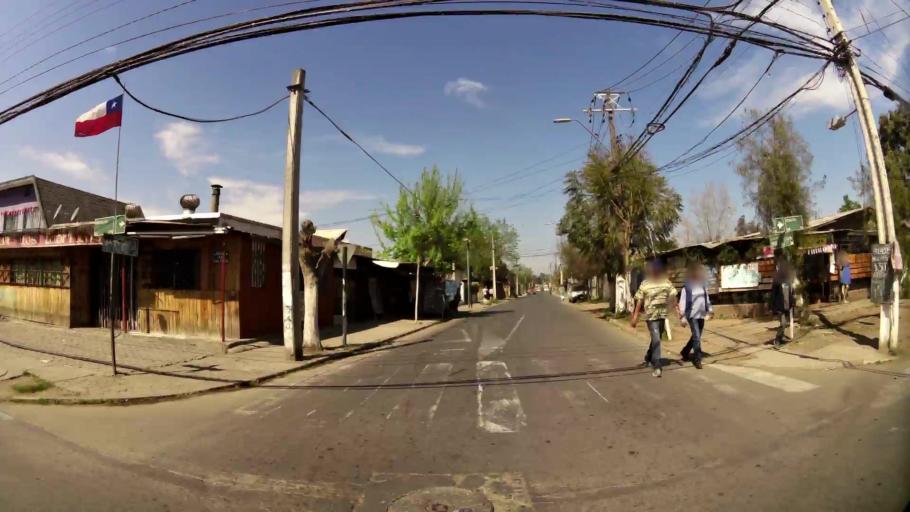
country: CL
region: Santiago Metropolitan
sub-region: Provincia de Santiago
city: Lo Prado
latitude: -33.4042
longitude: -70.7179
